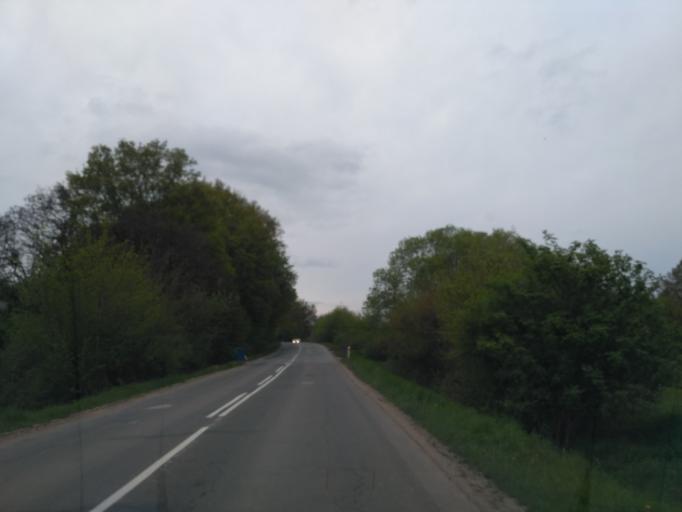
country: SK
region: Kosicky
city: Moldava nad Bodvou
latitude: 48.6555
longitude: 21.0032
